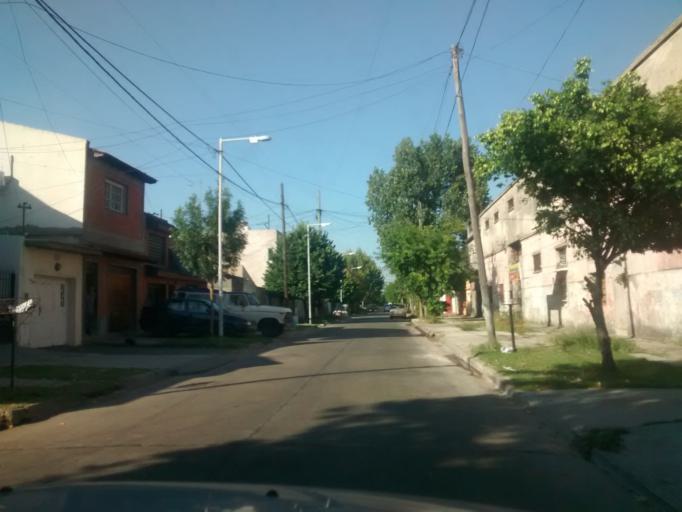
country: AR
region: Buenos Aires
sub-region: Partido de Avellaneda
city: Avellaneda
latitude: -34.6832
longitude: -58.3523
